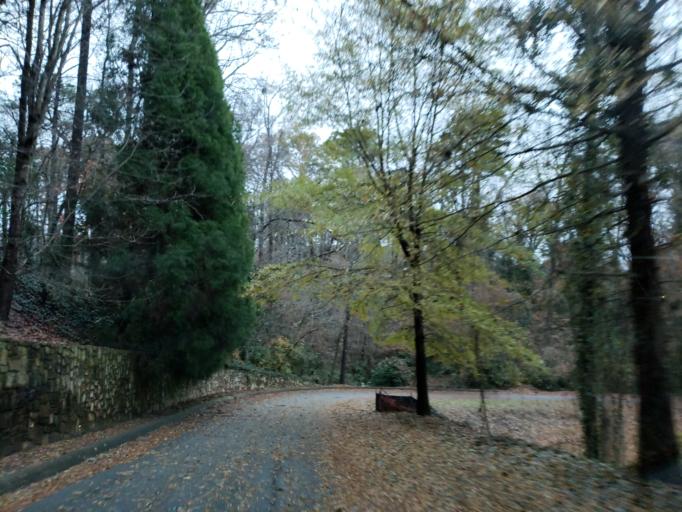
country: US
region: Georgia
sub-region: Cobb County
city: Vinings
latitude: 33.8750
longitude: -84.4132
